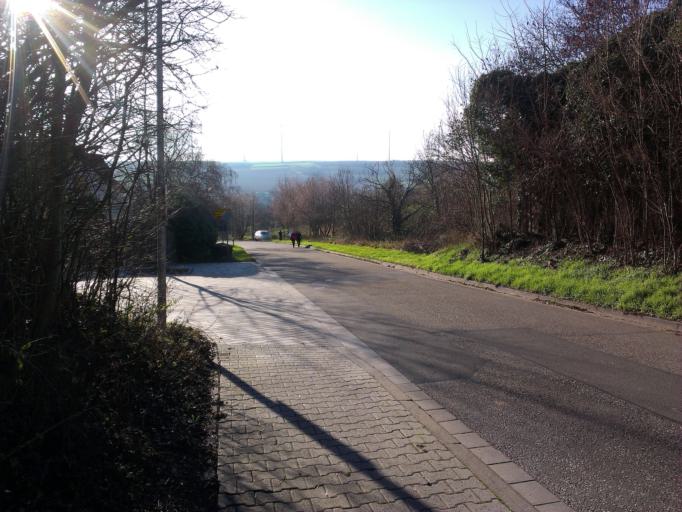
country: DE
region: Rheinland-Pfalz
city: Molsheim
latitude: 49.6462
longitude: 8.1712
